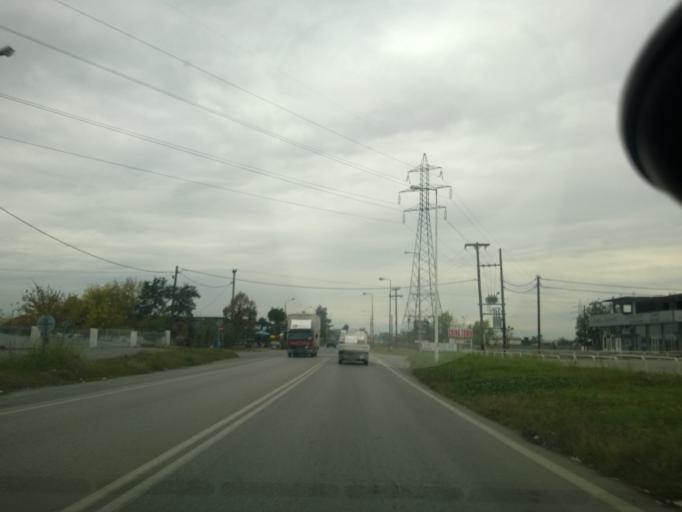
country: GR
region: Central Macedonia
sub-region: Nomos Pellis
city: Giannitsa
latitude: 40.7814
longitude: 22.3826
